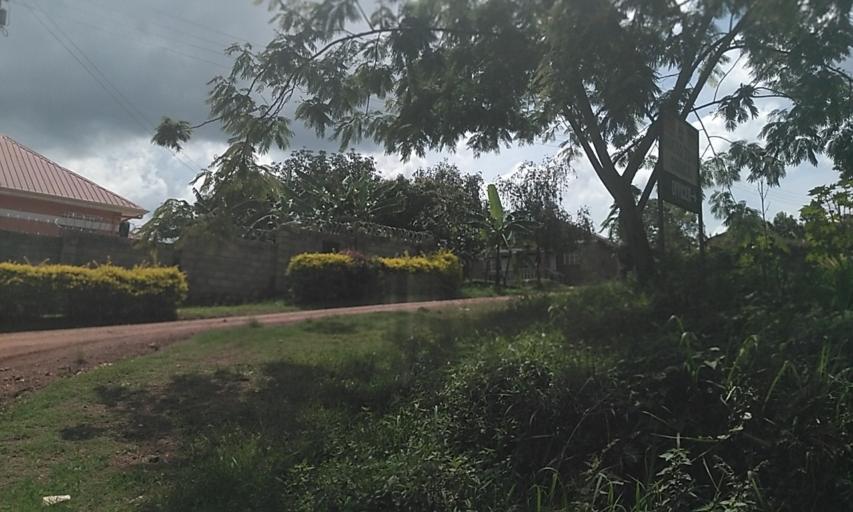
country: UG
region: Central Region
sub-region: Wakiso District
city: Wakiso
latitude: 0.3932
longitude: 32.4628
